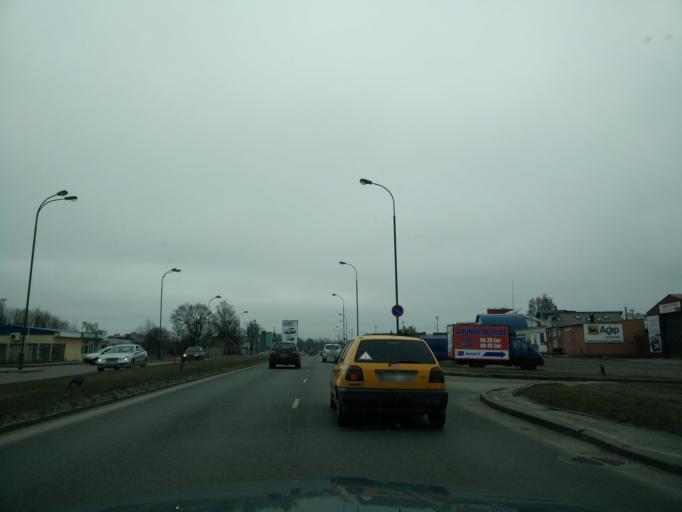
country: LT
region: Klaipedos apskritis
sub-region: Klaipeda
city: Klaipeda
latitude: 55.6915
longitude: 21.1431
